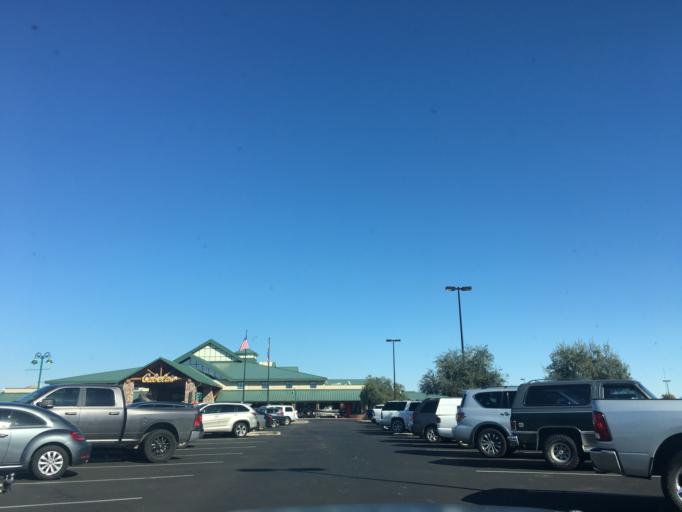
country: US
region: Arizona
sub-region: Maricopa County
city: Peoria
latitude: 33.5384
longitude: -112.2624
